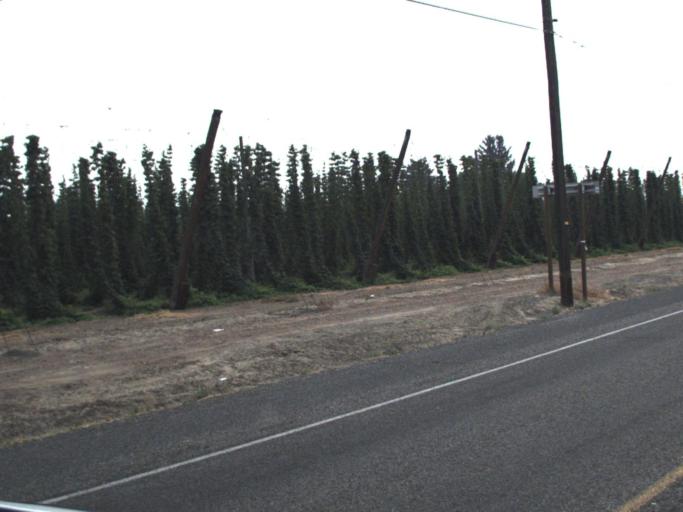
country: US
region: Washington
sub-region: Yakima County
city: Mabton
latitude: 46.2503
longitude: -119.9995
